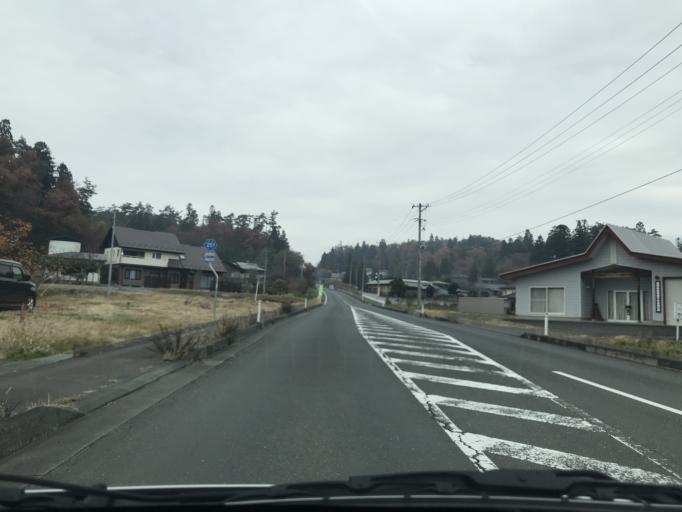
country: JP
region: Iwate
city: Mizusawa
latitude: 39.1612
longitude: 141.2014
